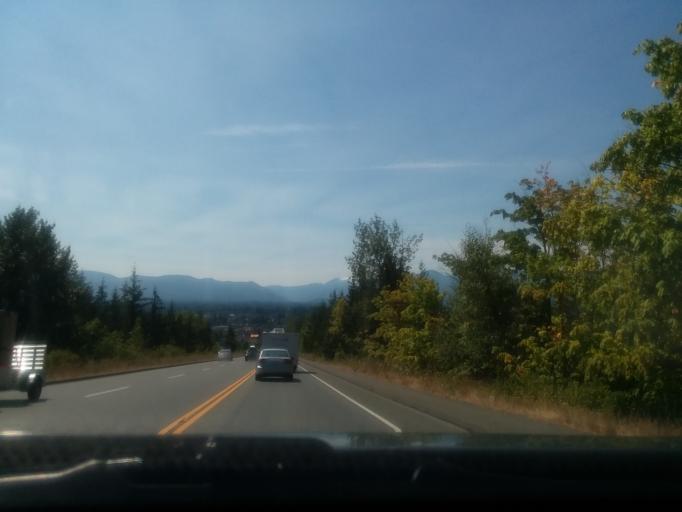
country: CA
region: British Columbia
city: Courtenay
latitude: 49.7043
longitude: -124.9773
